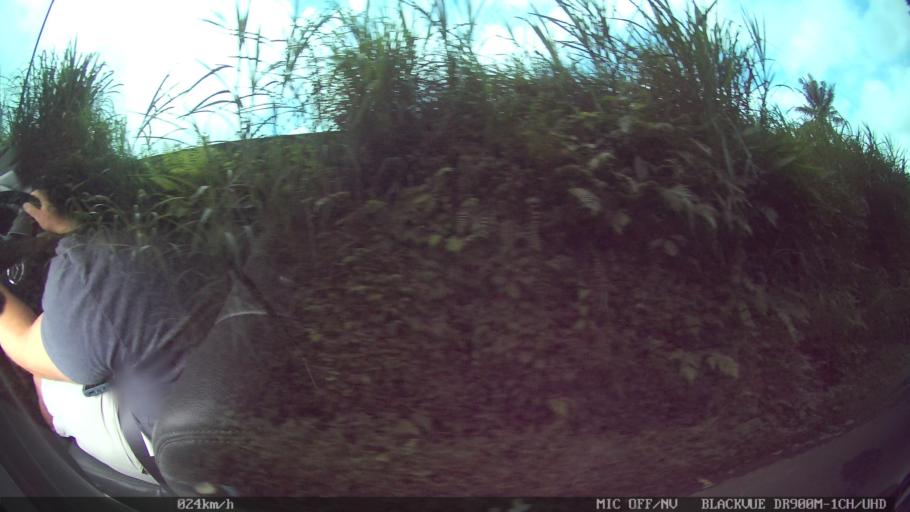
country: ID
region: Bali
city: Banjar Petak
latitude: -8.4442
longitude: 115.3226
